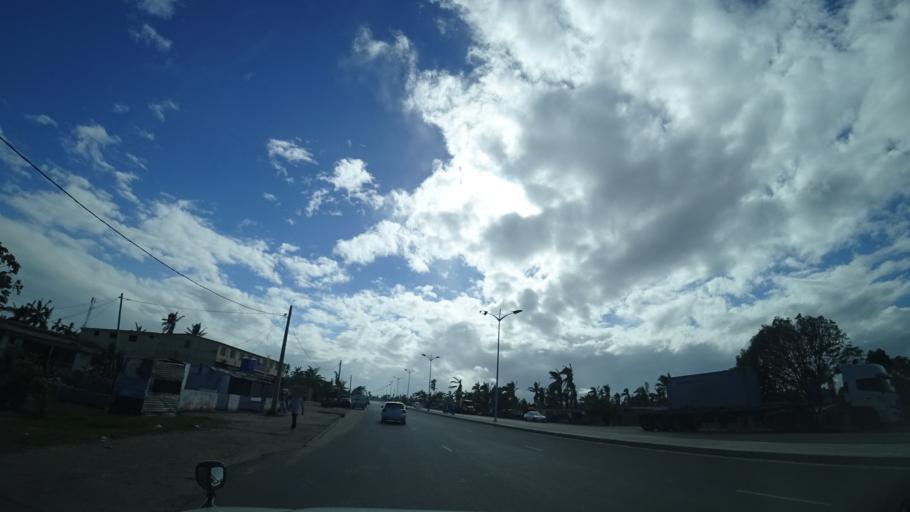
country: MZ
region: Sofala
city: Beira
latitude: -19.7809
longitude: 34.8795
